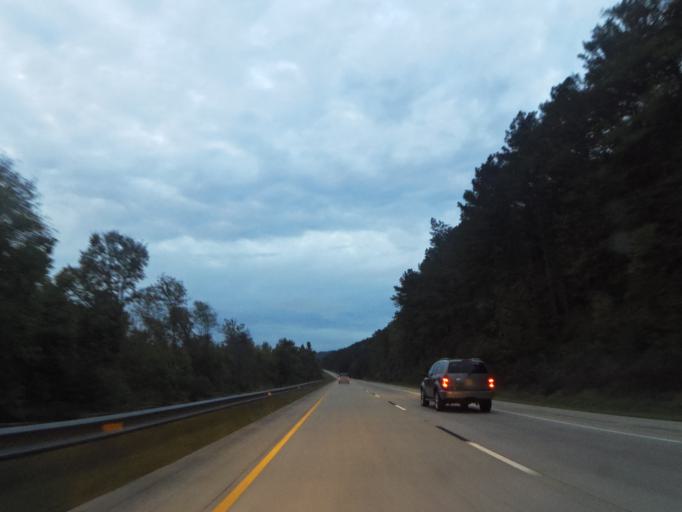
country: US
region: Alabama
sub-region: Etowah County
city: Gadsden
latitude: 34.1021
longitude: -85.9998
